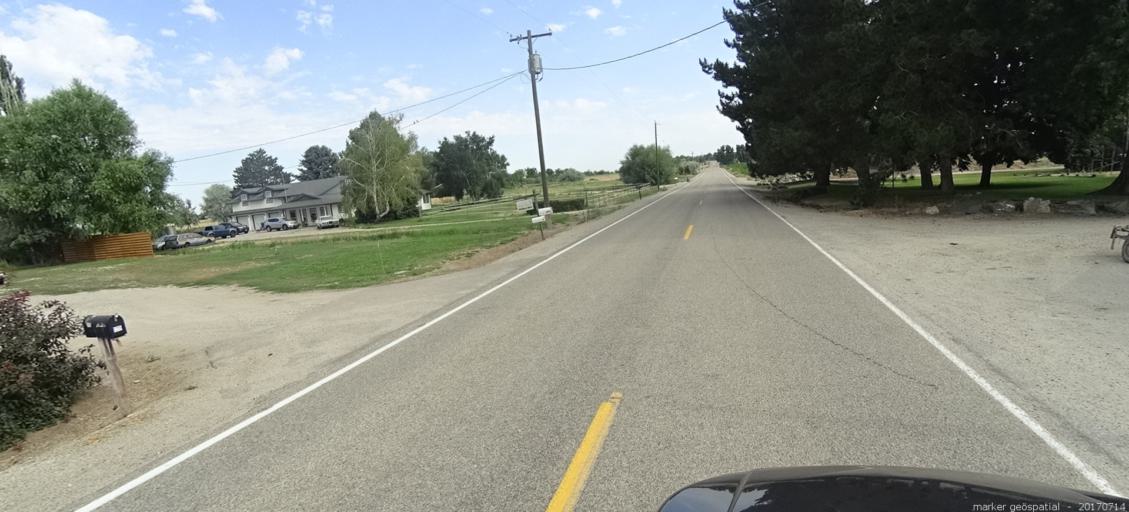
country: US
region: Idaho
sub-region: Ada County
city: Kuna
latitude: 43.4770
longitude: -116.3545
